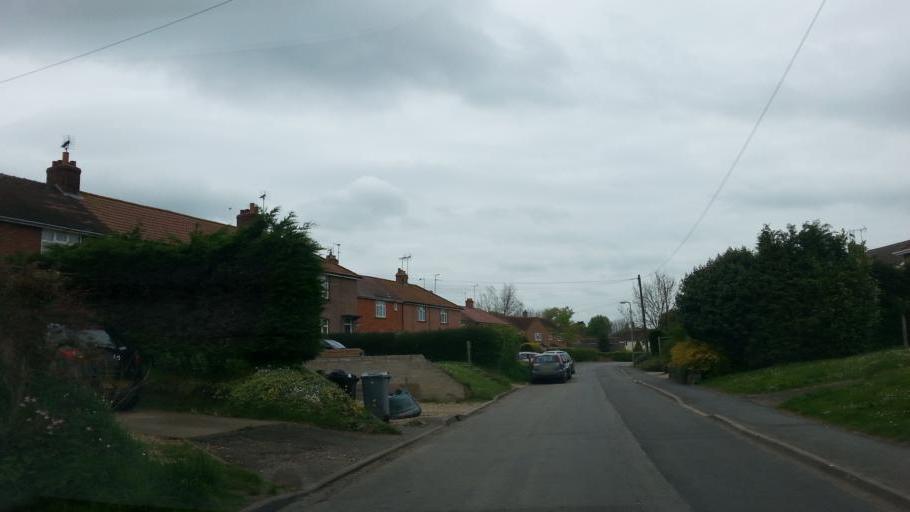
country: GB
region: England
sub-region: Lincolnshire
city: Bourne
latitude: 52.7404
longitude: -0.3824
